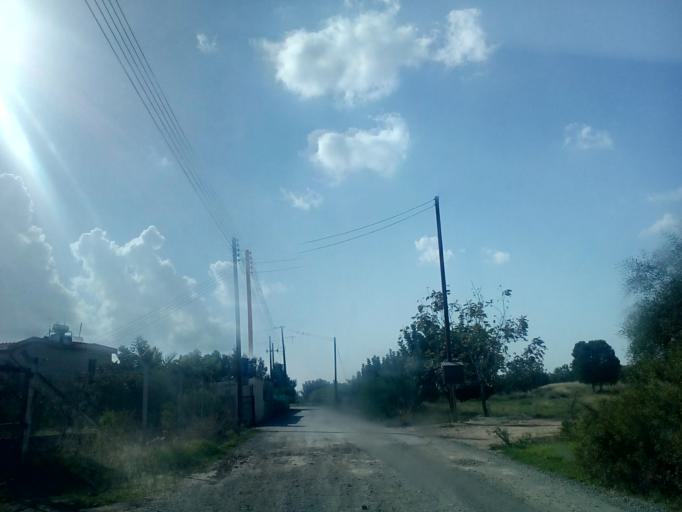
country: CY
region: Limassol
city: Ypsonas
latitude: 34.6741
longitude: 32.9714
